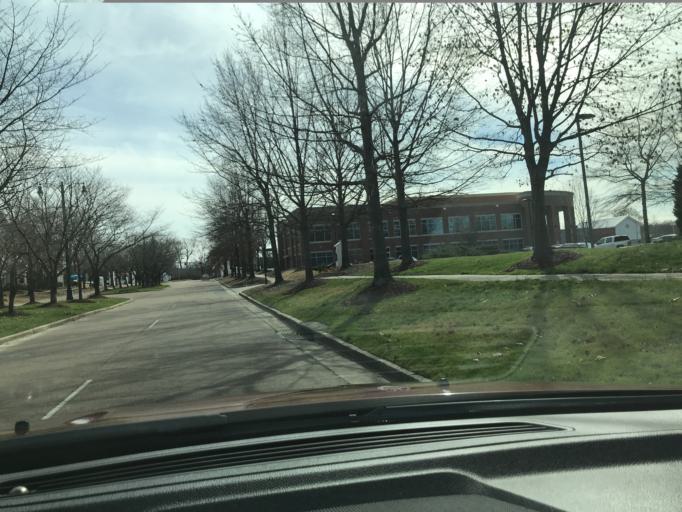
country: US
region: Tennessee
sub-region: Shelby County
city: Collierville
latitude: 35.0398
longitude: -89.7033
